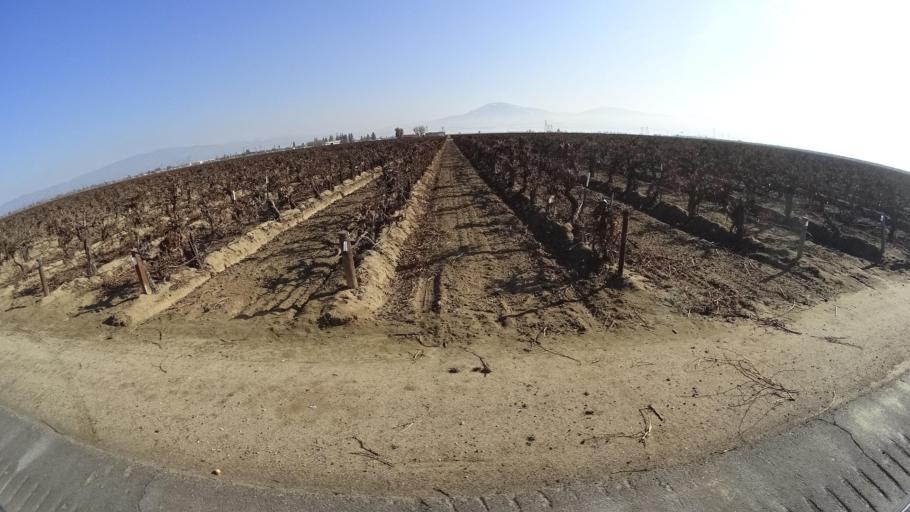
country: US
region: California
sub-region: Kern County
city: Weedpatch
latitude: 35.2350
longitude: -118.9322
